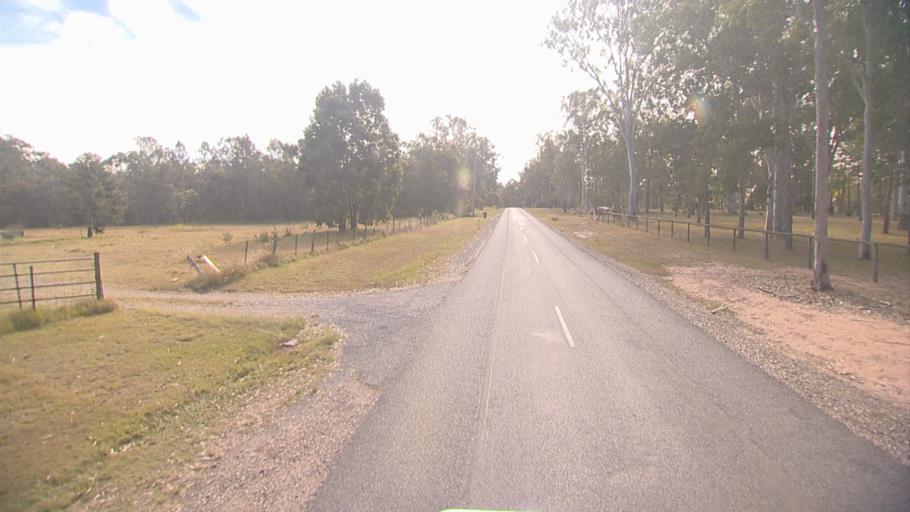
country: AU
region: Queensland
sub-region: Logan
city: North Maclean
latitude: -27.7501
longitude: 152.9735
